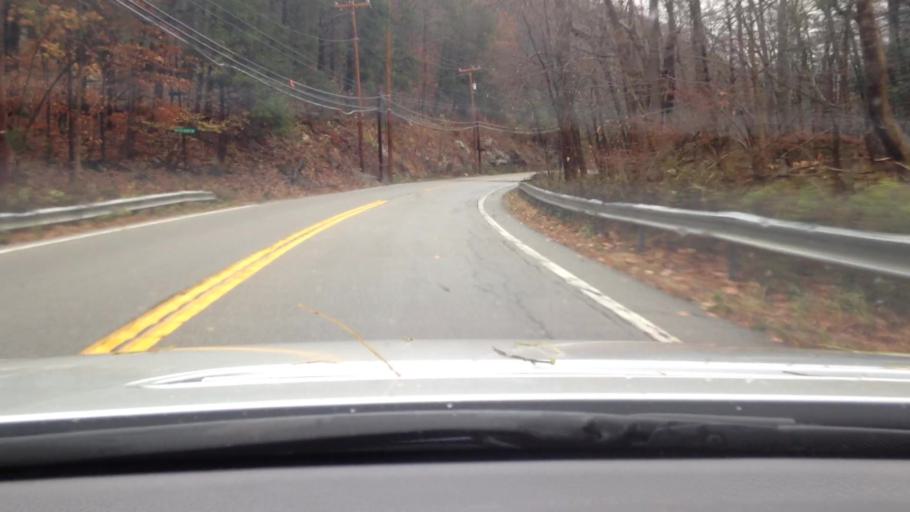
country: US
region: New York
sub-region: Orange County
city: Highland Falls
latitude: 41.3630
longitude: -73.9261
